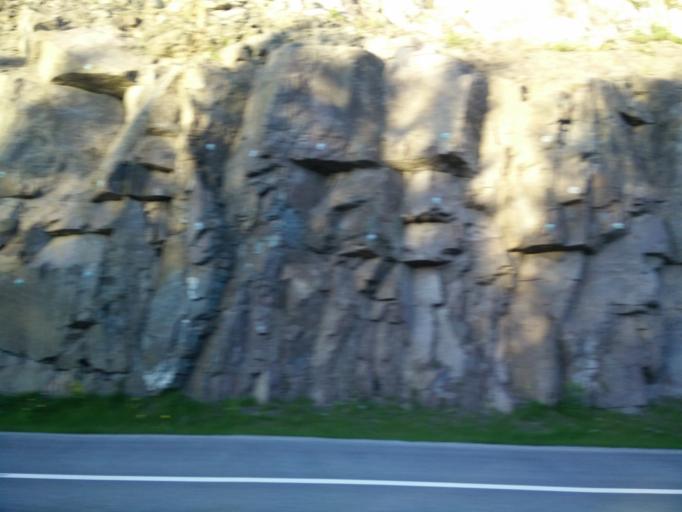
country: NO
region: Akershus
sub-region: Baerum
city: Skui
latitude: 59.9675
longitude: 10.3410
